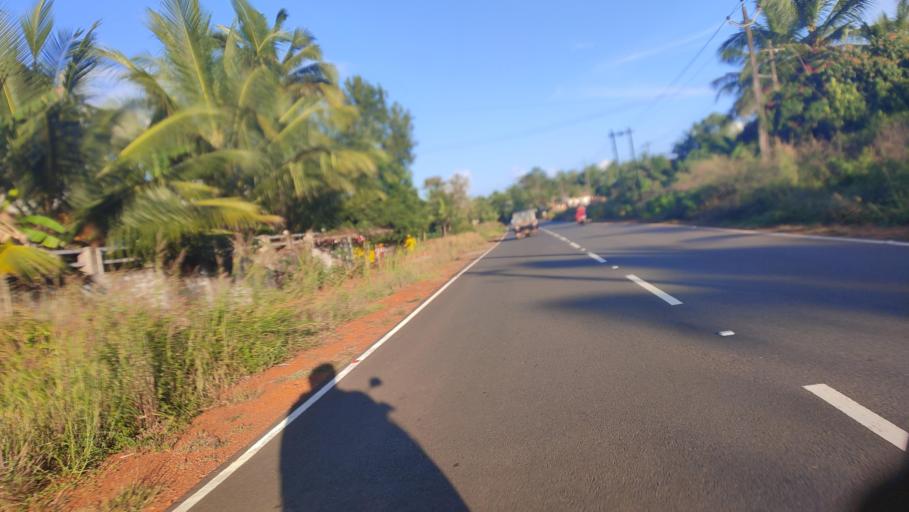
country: IN
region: Kerala
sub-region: Kasaragod District
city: Kasaragod
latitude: 12.4650
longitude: 75.0742
